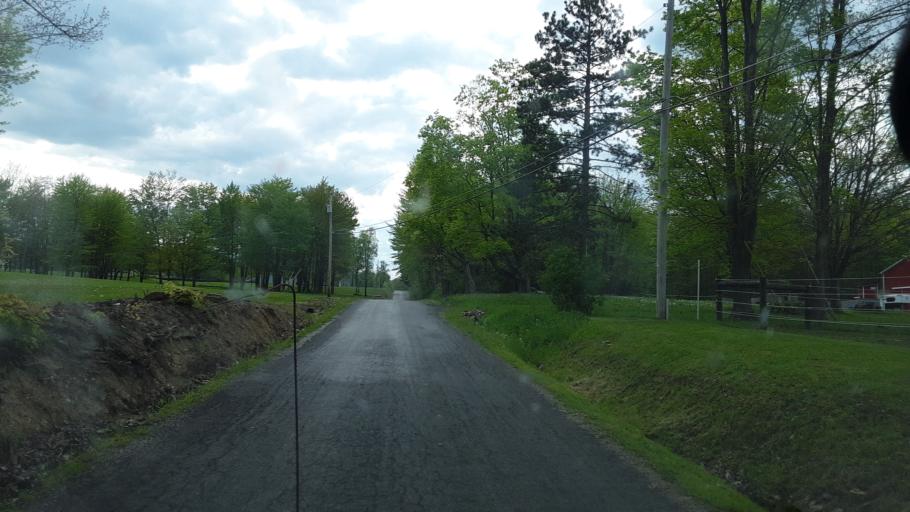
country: US
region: Ohio
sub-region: Portage County
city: Garrettsville
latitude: 41.3428
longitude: -81.0460
